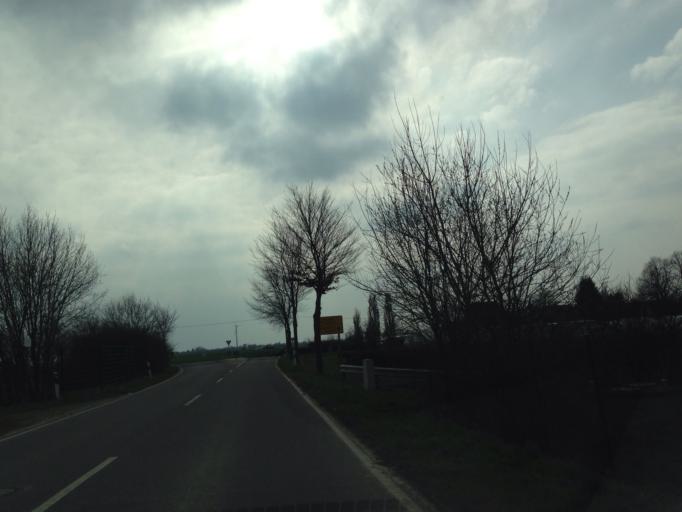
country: DE
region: North Rhine-Westphalia
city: Huckelhoven
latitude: 51.0851
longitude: 6.2575
